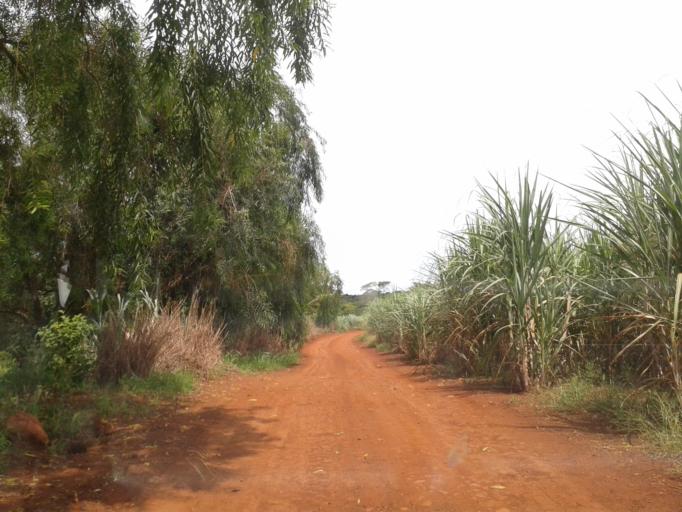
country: BR
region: Minas Gerais
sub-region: Centralina
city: Centralina
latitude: -18.5888
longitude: -49.2696
